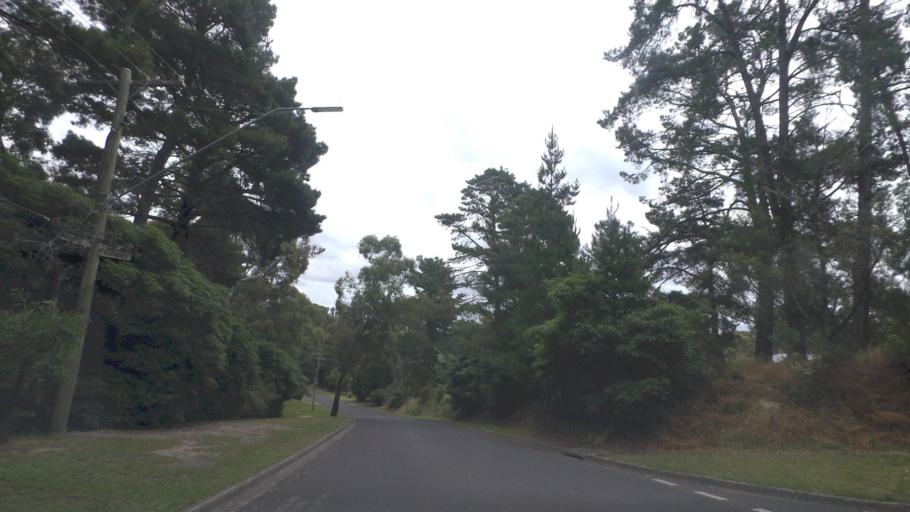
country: AU
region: Victoria
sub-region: Manningham
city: Park Orchards
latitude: -37.7811
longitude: 145.2146
